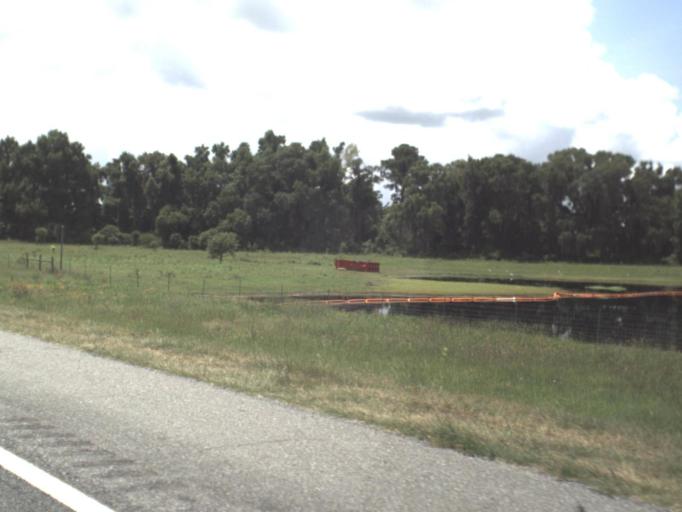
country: US
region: Florida
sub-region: Suwannee County
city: Wellborn
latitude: 30.2388
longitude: -82.7378
